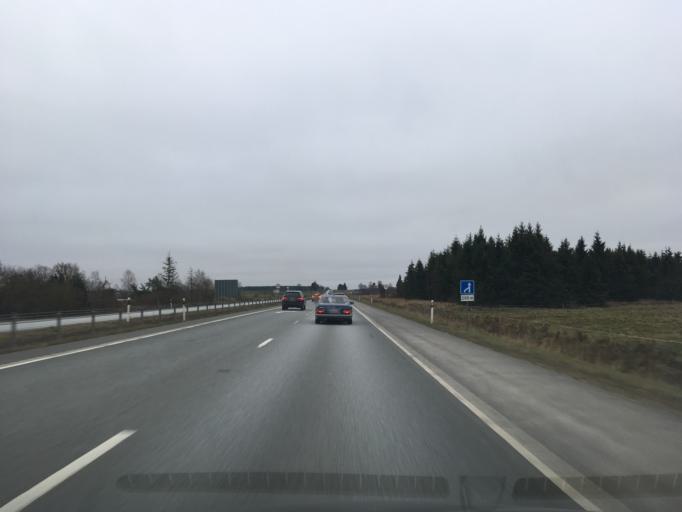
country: EE
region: Laeaene-Virumaa
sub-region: Haljala vald
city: Haljala
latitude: 59.4222
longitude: 26.2849
